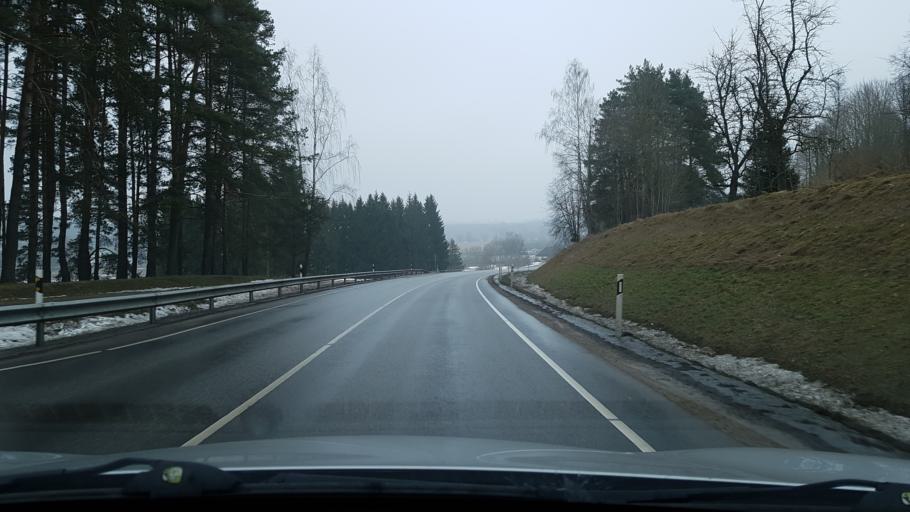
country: EE
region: Viljandimaa
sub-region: Viiratsi vald
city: Viiratsi
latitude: 58.3590
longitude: 25.6299
